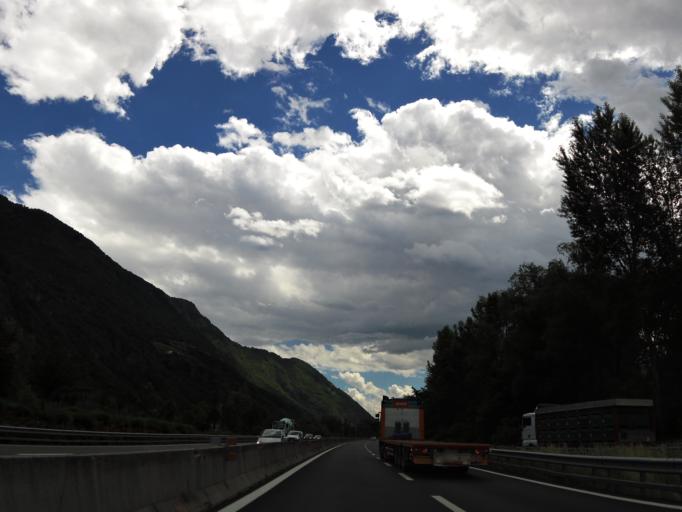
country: IT
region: Trentino-Alto Adige
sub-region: Bolzano
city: Sinigo
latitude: 46.6282
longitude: 11.1788
